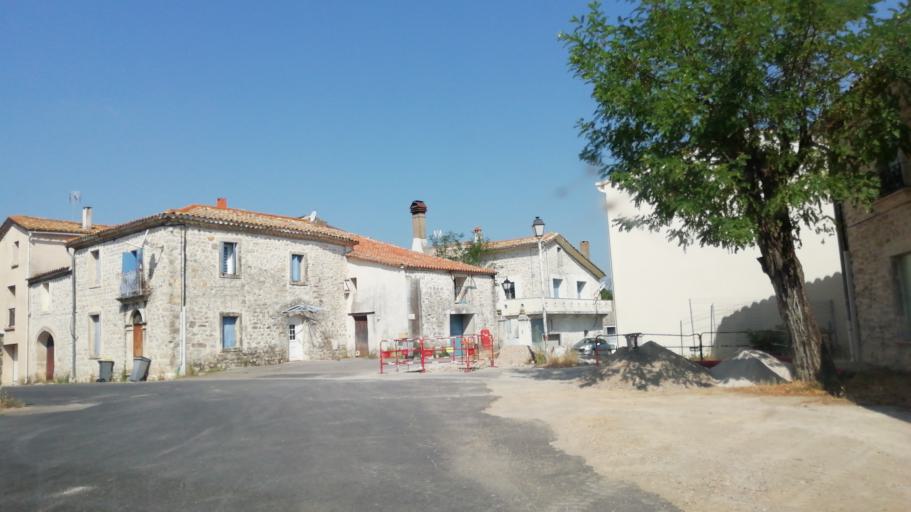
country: FR
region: Languedoc-Roussillon
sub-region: Departement de l'Herault
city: Saint-Mathieu-de-Treviers
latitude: 43.7401
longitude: 3.8532
